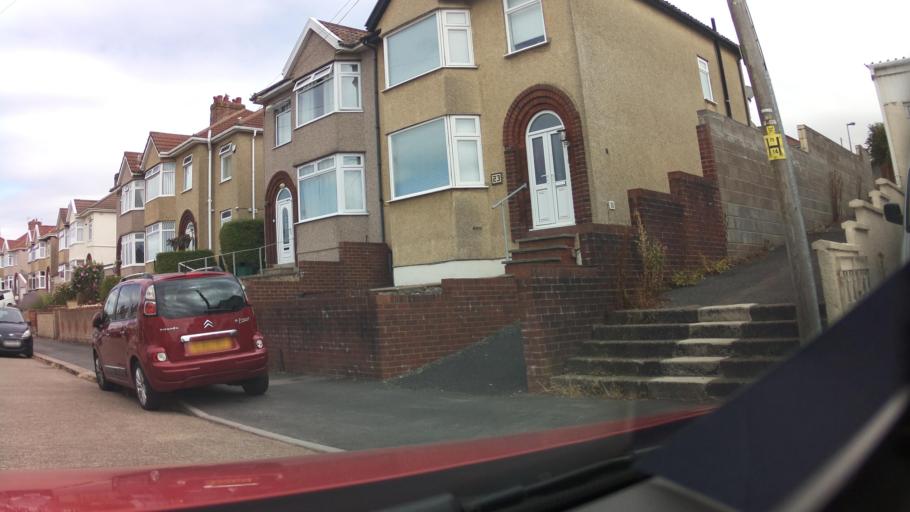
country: GB
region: England
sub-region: Bristol
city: Bristol
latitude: 51.4355
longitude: -2.5836
